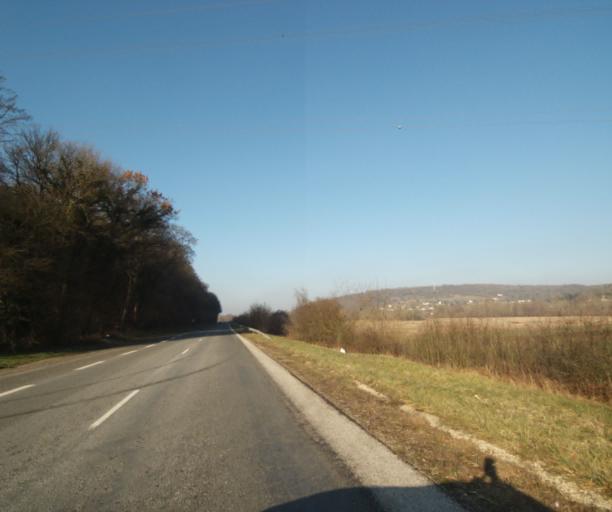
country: FR
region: Champagne-Ardenne
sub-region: Departement de la Haute-Marne
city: Chevillon
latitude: 48.5147
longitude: 5.1104
